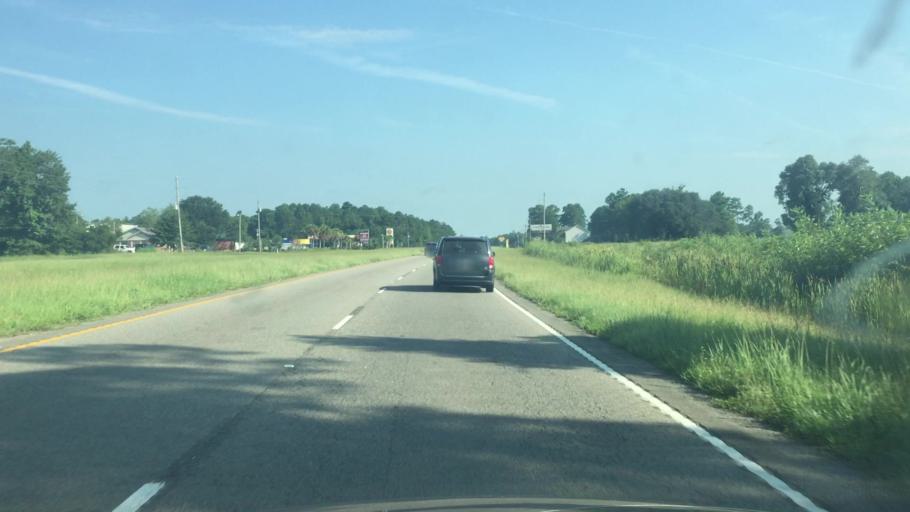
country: US
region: South Carolina
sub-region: Horry County
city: North Myrtle Beach
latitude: 33.9221
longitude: -78.7252
